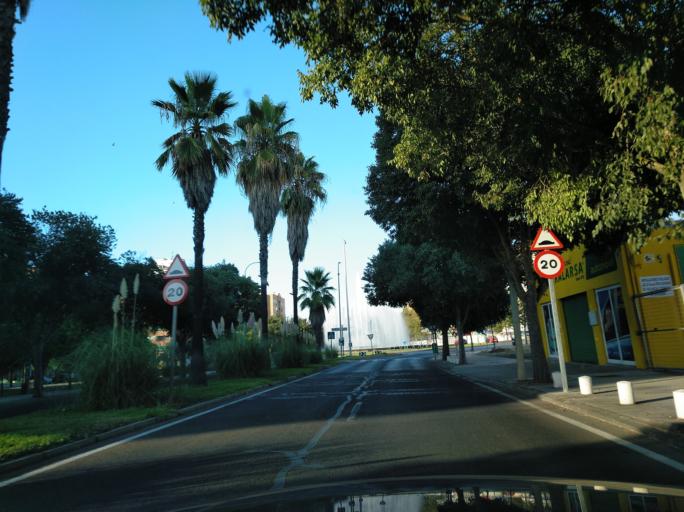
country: ES
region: Extremadura
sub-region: Provincia de Badajoz
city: Badajoz
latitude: 38.8644
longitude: -6.9835
